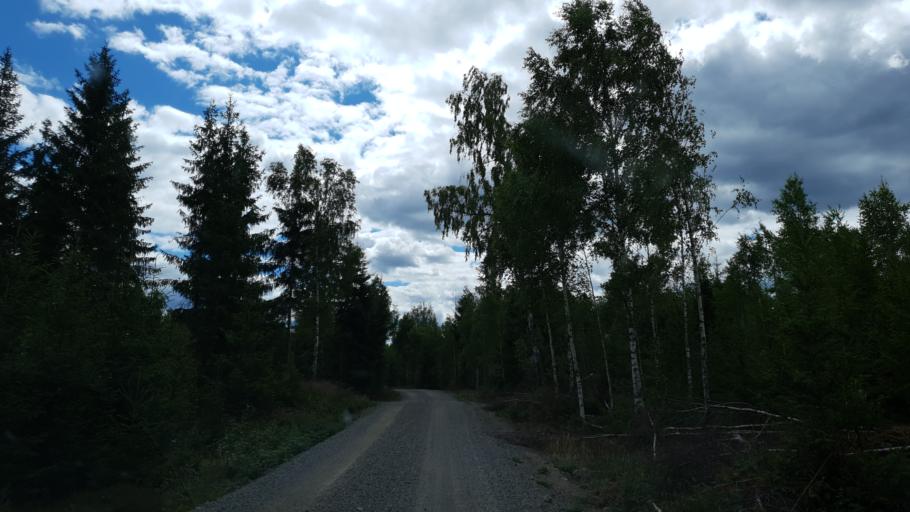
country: SE
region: Kalmar
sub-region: Hultsfreds Kommun
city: Virserum
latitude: 57.0885
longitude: 15.6209
